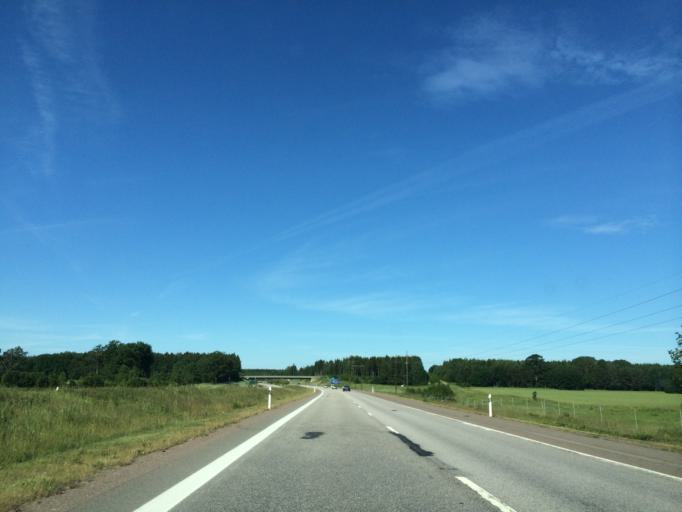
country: SE
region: OEstergoetland
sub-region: Boxholms Kommun
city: Boxholm
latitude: 58.3020
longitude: 14.9542
